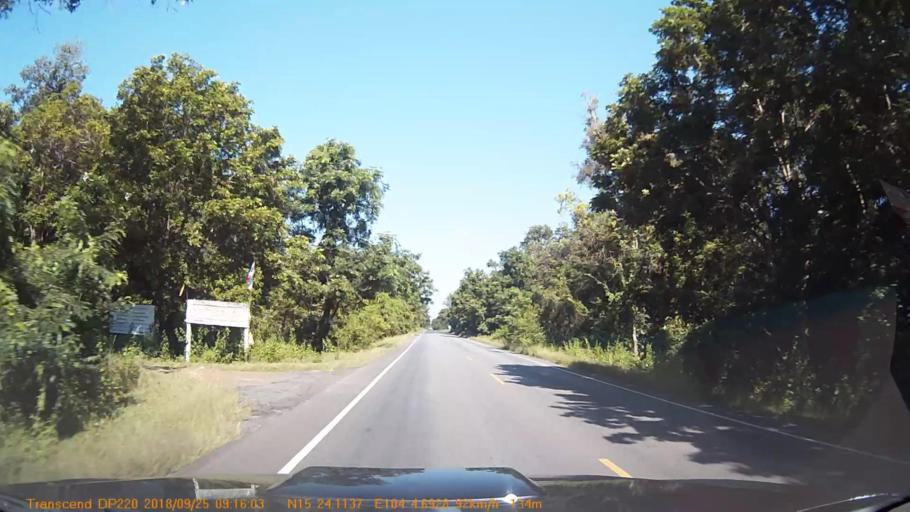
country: TH
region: Sisaket
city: Sila Lat
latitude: 15.4018
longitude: 104.0784
